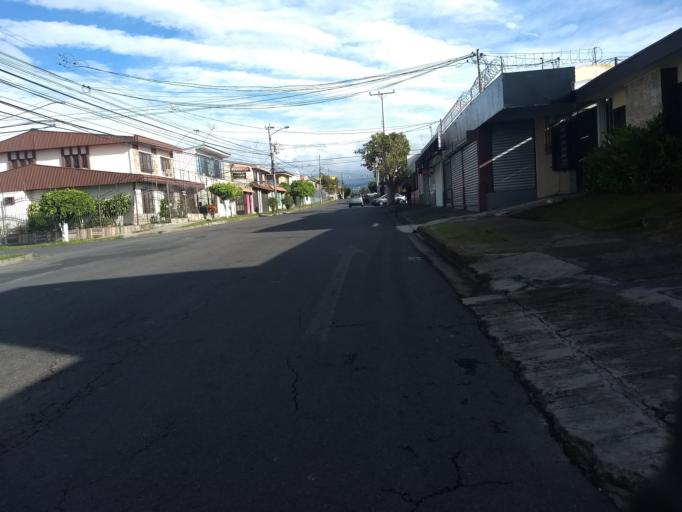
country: CR
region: San Jose
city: San Juan
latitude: 9.9602
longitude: -84.0853
